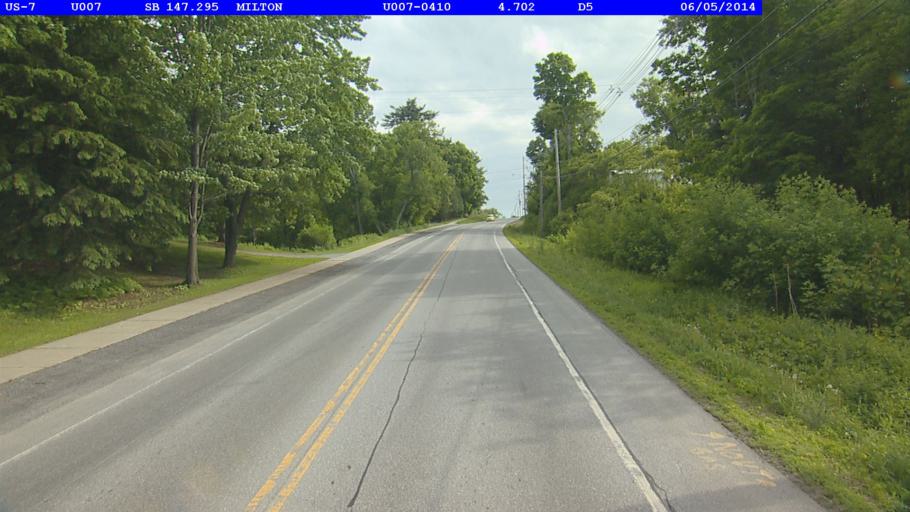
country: US
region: Vermont
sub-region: Chittenden County
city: Milton
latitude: 44.6351
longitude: -73.1140
